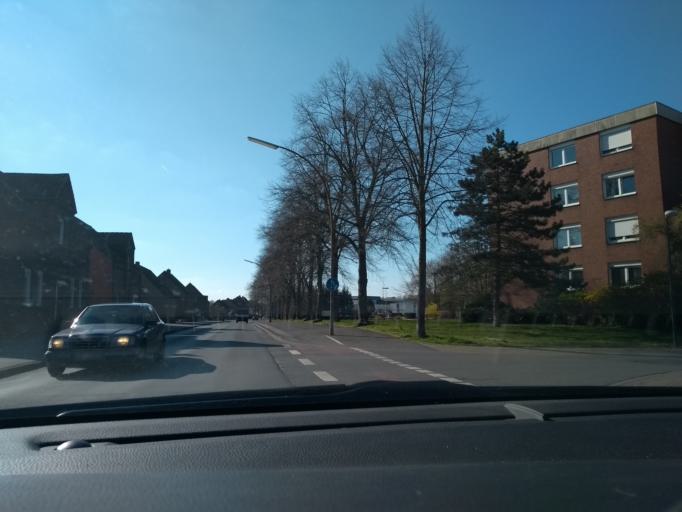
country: DE
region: North Rhine-Westphalia
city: Lunen
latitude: 51.6240
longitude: 7.5067
